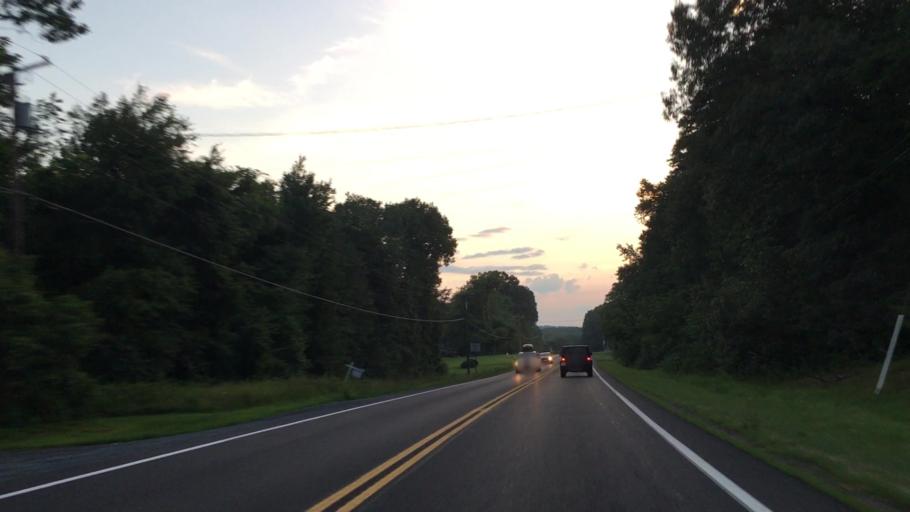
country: US
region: Virginia
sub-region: Orange County
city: Orange
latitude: 38.2582
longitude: -77.9988
